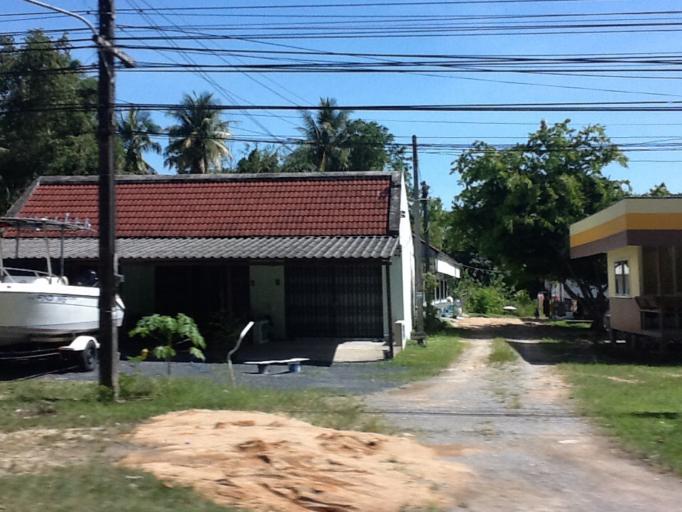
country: TH
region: Phuket
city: Thalang
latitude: 8.0284
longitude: 98.4013
